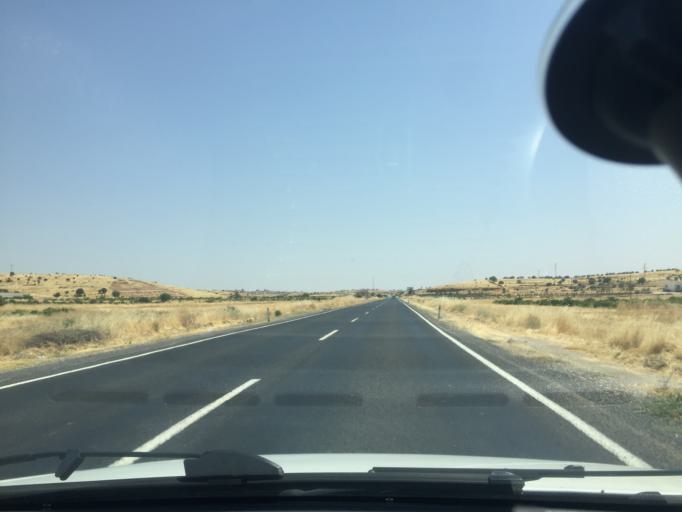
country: TR
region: Mardin
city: Kindirip
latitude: 37.4535
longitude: 41.2540
